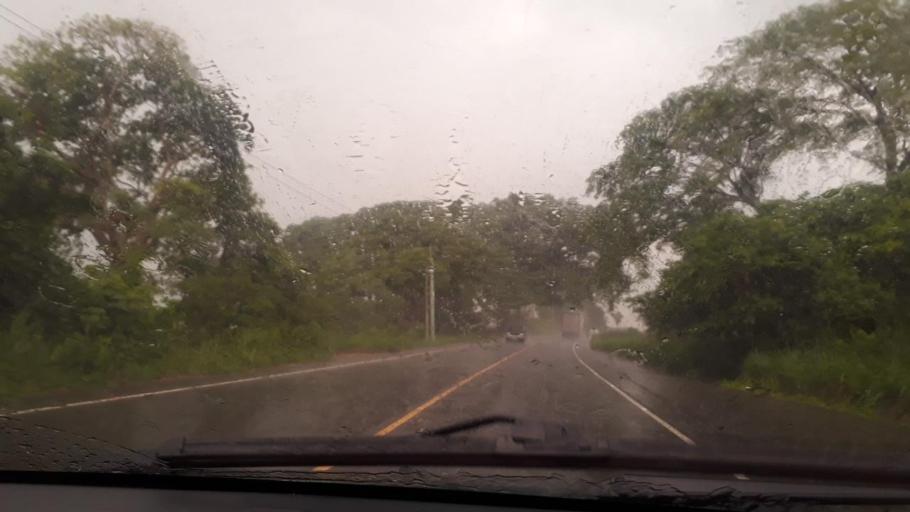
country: GT
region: Santa Rosa
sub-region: Municipio de Taxisco
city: Taxisco
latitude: 14.0942
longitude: -90.5254
